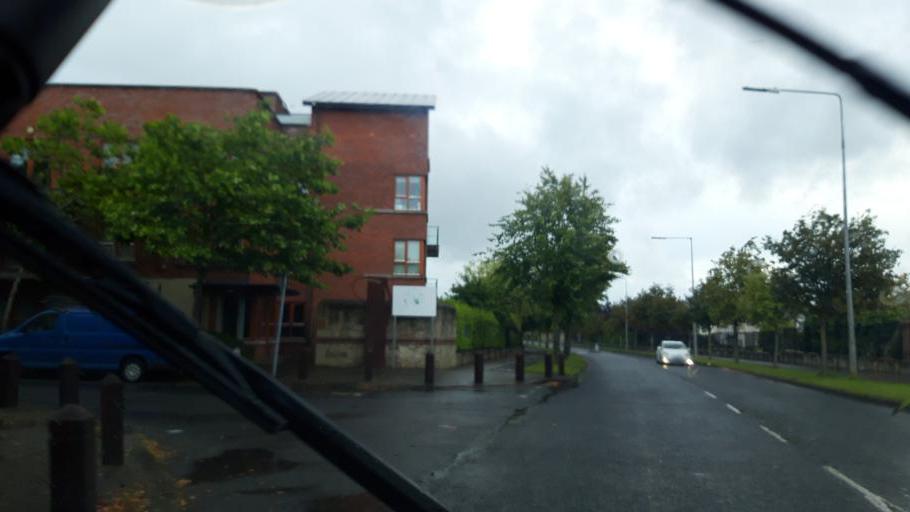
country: IE
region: Leinster
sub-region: Fingal County
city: Blanchardstown
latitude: 53.3732
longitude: -6.4001
